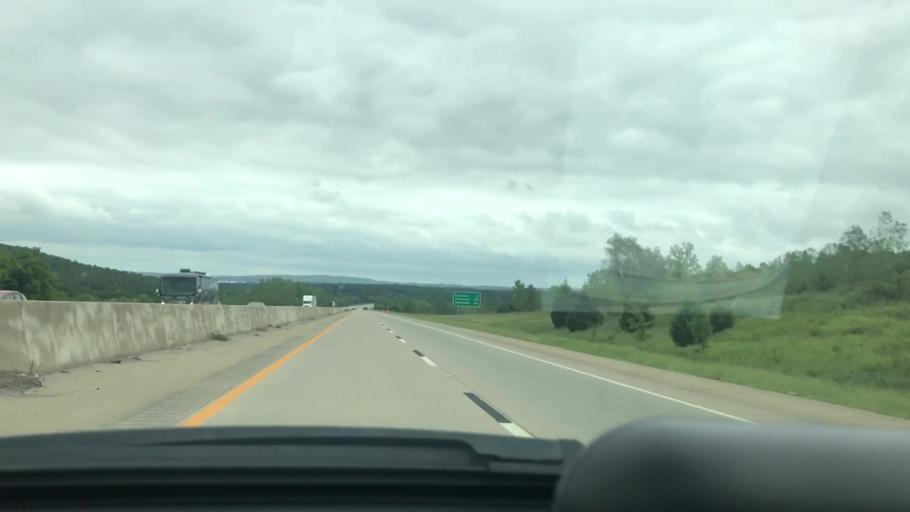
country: US
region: Oklahoma
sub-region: McIntosh County
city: Eufaula
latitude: 35.1821
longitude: -95.6432
